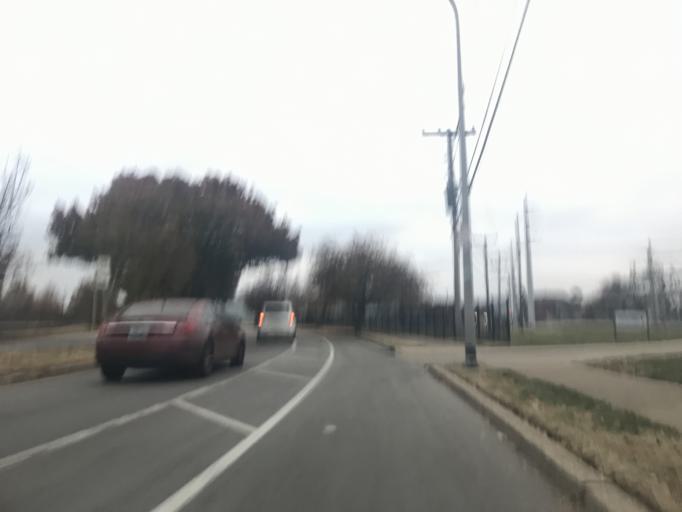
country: US
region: Kentucky
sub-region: Jefferson County
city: Louisville
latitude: 38.2502
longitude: -85.7730
